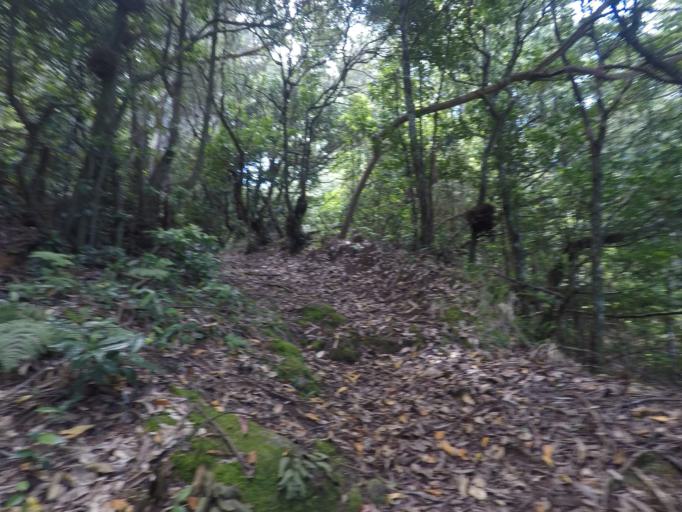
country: PT
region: Madeira
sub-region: Porto Moniz
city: Porto Moniz
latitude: 32.8348
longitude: -17.1407
